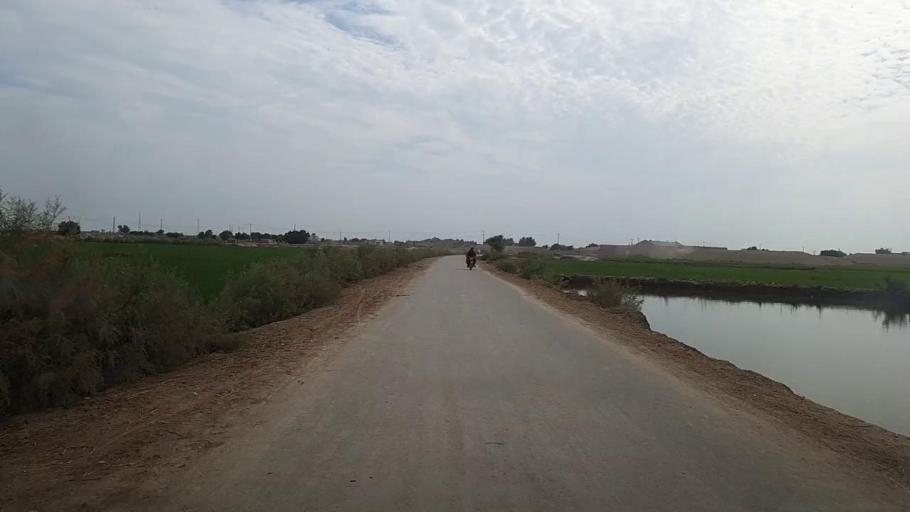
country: PK
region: Sindh
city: Thul
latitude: 28.2600
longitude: 68.7769
